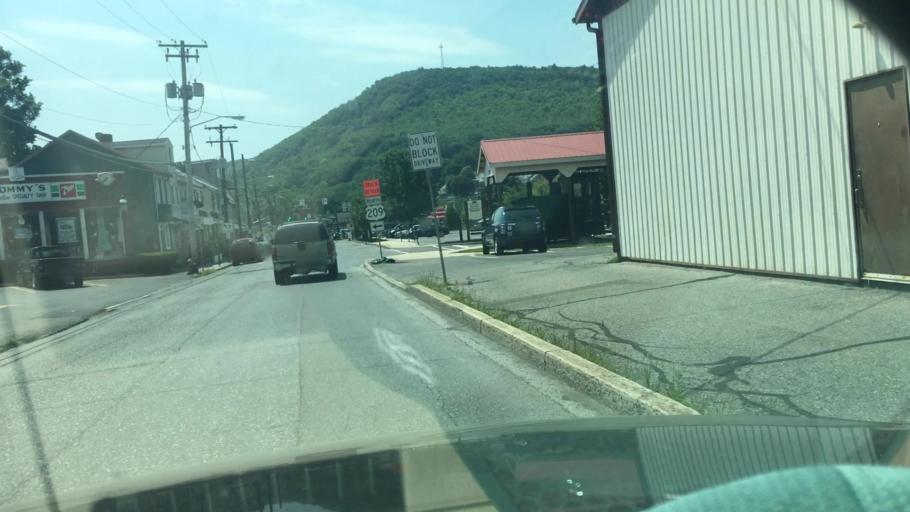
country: US
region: Pennsylvania
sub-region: Schuylkill County
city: Tamaqua
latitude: 40.7990
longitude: -75.9696
